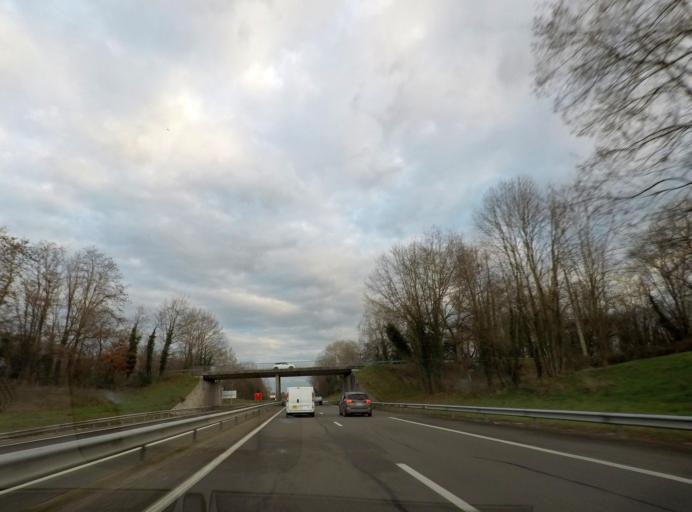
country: FR
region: Rhone-Alpes
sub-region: Departement de l'Ain
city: Crottet
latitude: 46.2926
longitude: 4.9141
